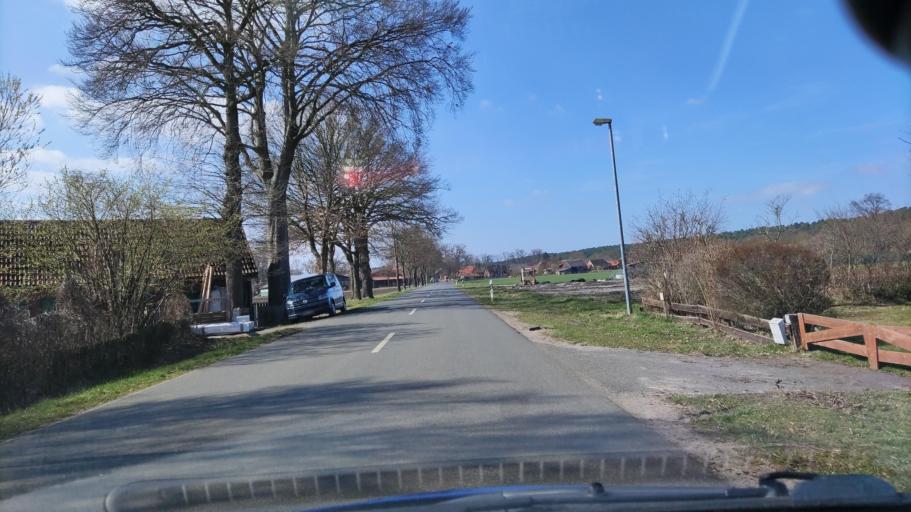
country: DE
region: Lower Saxony
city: Klein Gusborn
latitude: 53.0748
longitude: 11.2219
